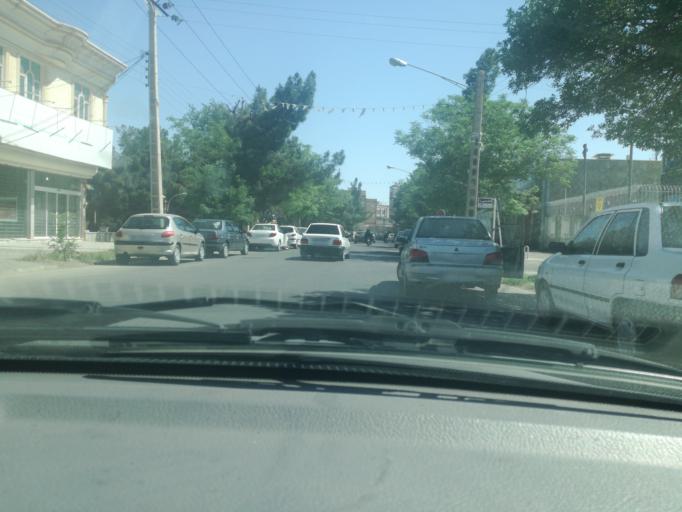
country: IR
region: Razavi Khorasan
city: Sarakhs
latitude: 36.5344
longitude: 61.1621
